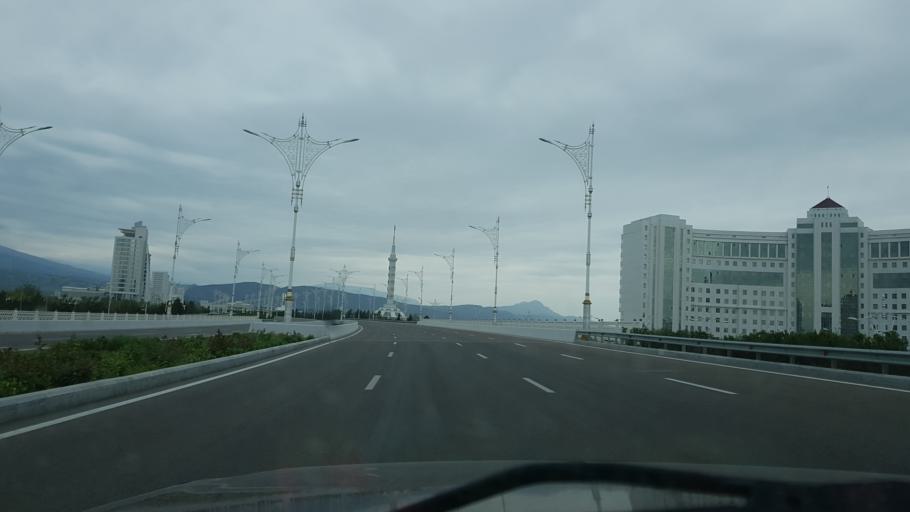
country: TM
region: Ahal
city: Ashgabat
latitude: 37.8955
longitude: 58.3363
